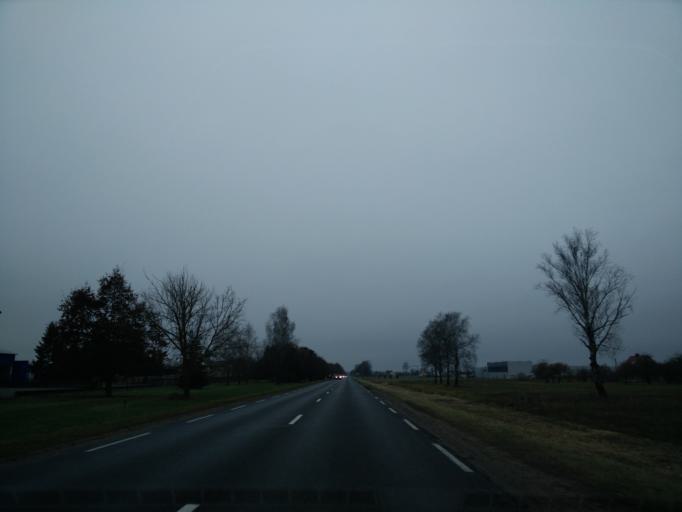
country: LT
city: Ariogala
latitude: 55.2596
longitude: 23.4944
